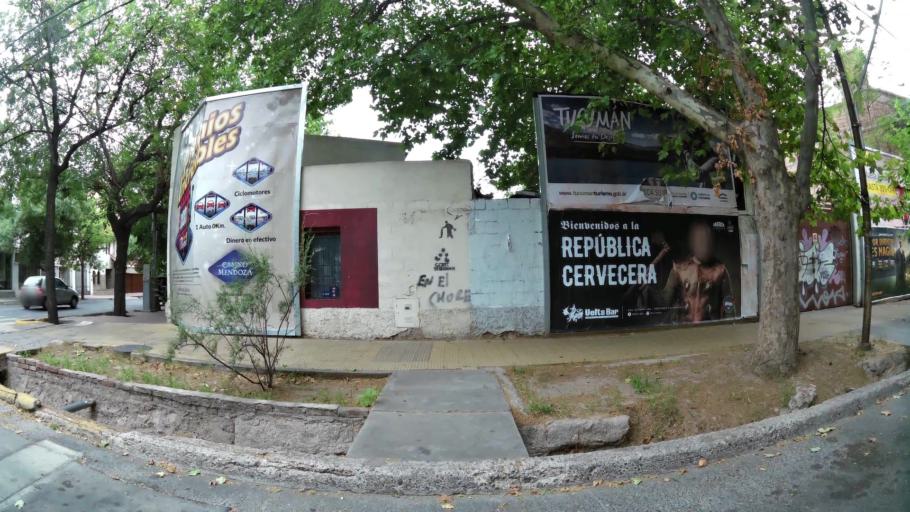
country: AR
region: Mendoza
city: Mendoza
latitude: -32.8907
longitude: -68.8621
